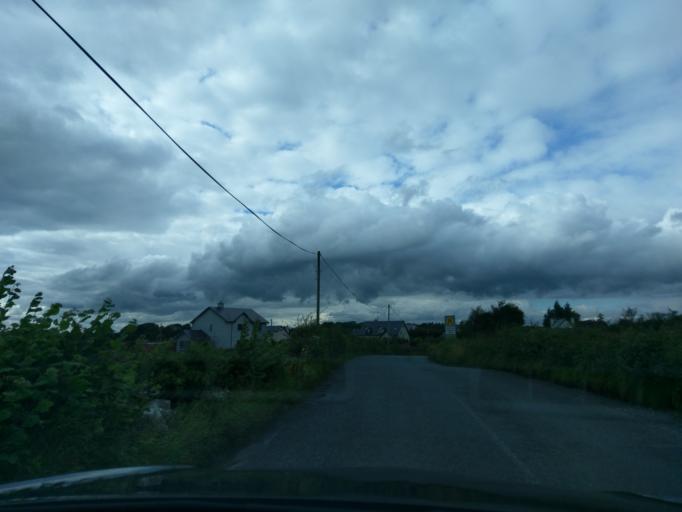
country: IE
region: Connaught
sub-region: County Galway
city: Athenry
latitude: 53.2487
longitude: -8.7486
